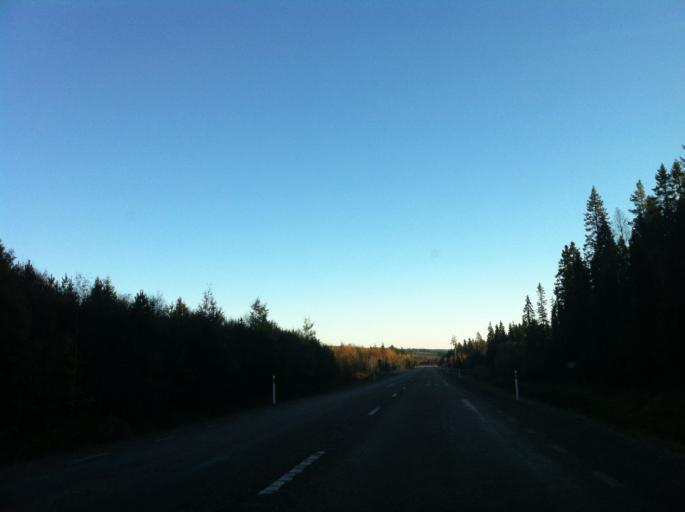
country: SE
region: Dalarna
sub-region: Rattviks Kommun
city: Raettvik
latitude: 60.8326
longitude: 15.2362
